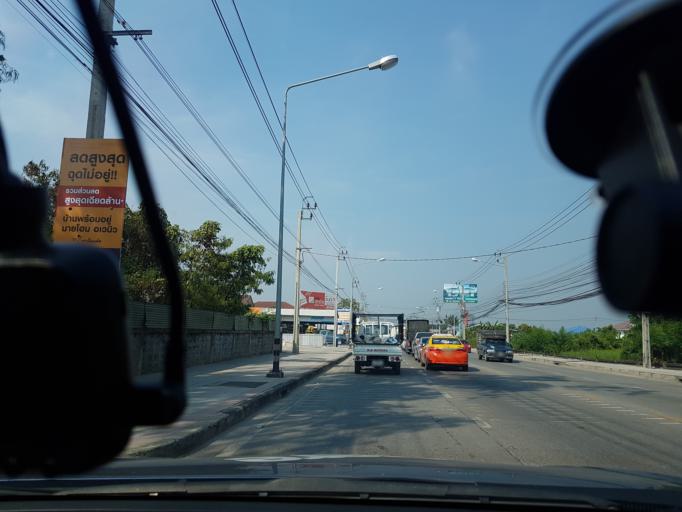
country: TH
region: Bangkok
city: Khlong Sam Wa
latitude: 13.8861
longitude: 100.7222
